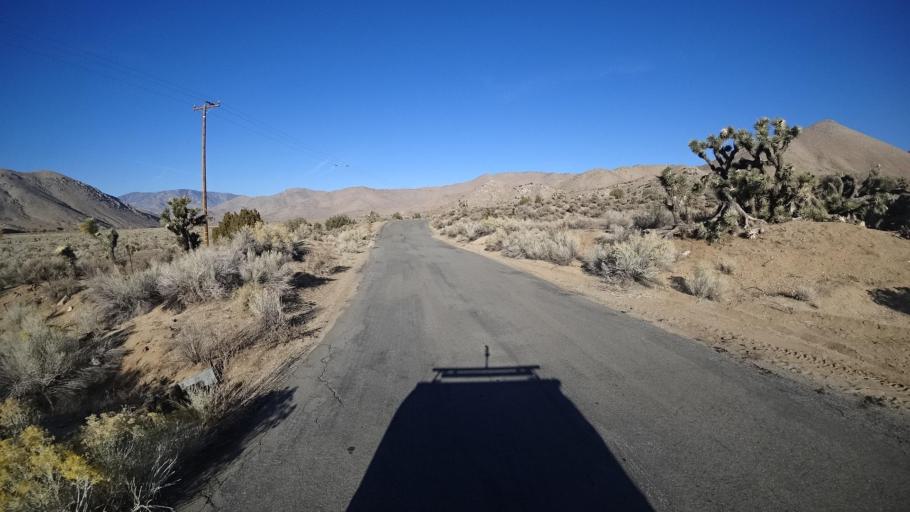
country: US
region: California
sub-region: Kern County
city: Weldon
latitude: 35.5835
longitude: -118.2462
